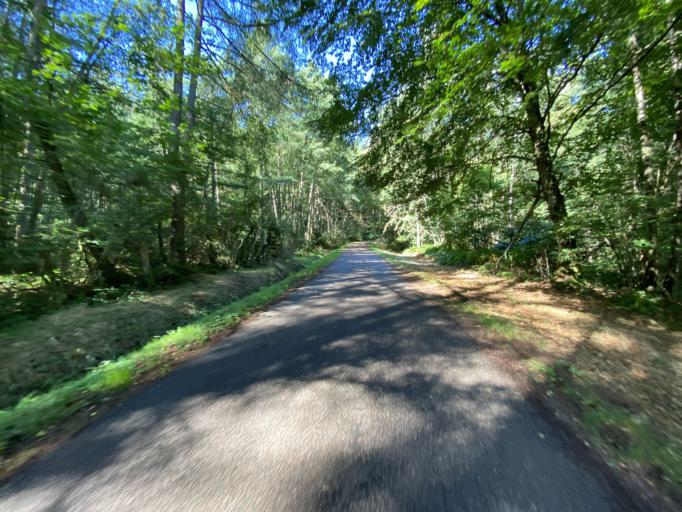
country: FR
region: Bourgogne
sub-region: Departement de la Cote-d'Or
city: Saulieu
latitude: 47.2757
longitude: 4.1668
